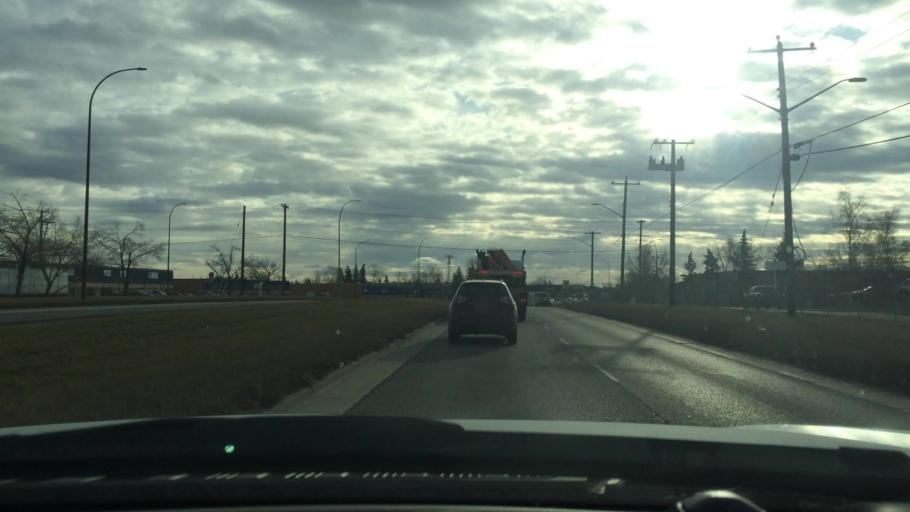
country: CA
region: Alberta
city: Calgary
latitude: 51.0024
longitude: -113.9899
